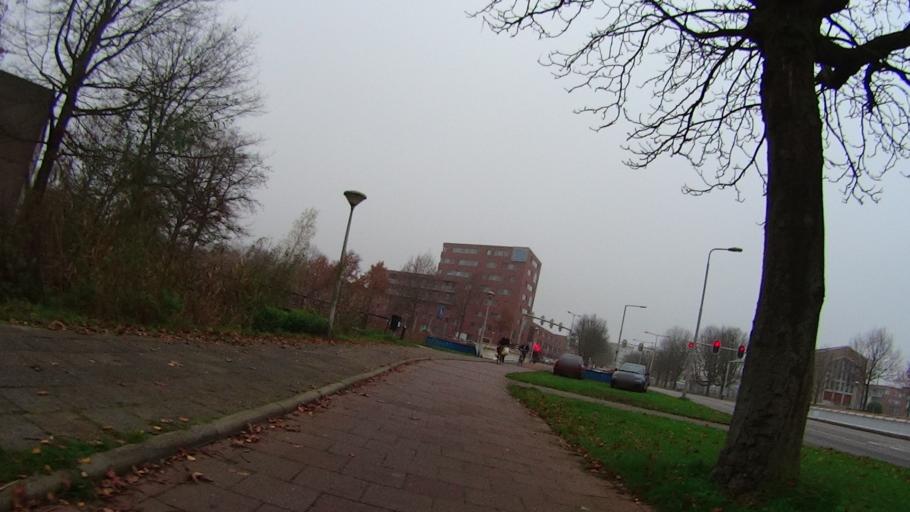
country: NL
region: Utrecht
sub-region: Gemeente Amersfoort
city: Randenbroek
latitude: 52.1636
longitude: 5.4043
